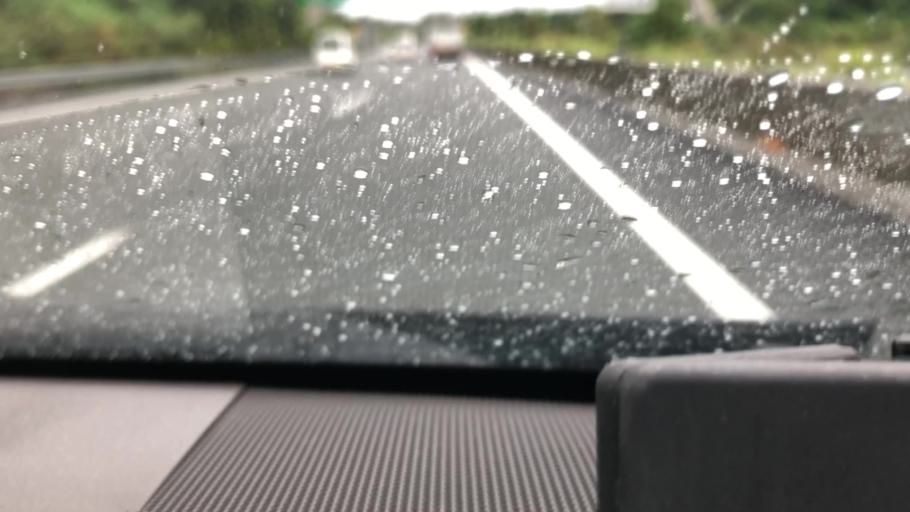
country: JP
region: Shizuoka
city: Mishima
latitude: 35.1693
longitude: 138.8818
